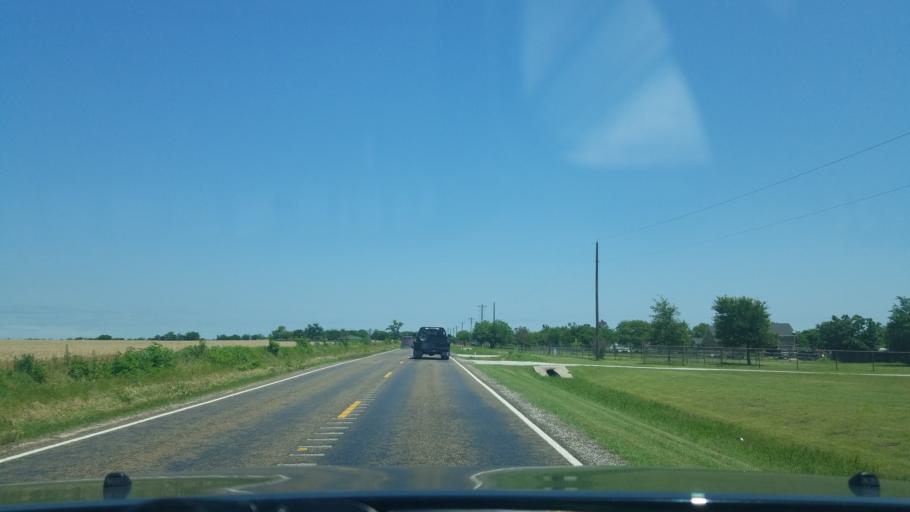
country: US
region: Texas
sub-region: Denton County
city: Krum
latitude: 33.2718
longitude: -97.2356
